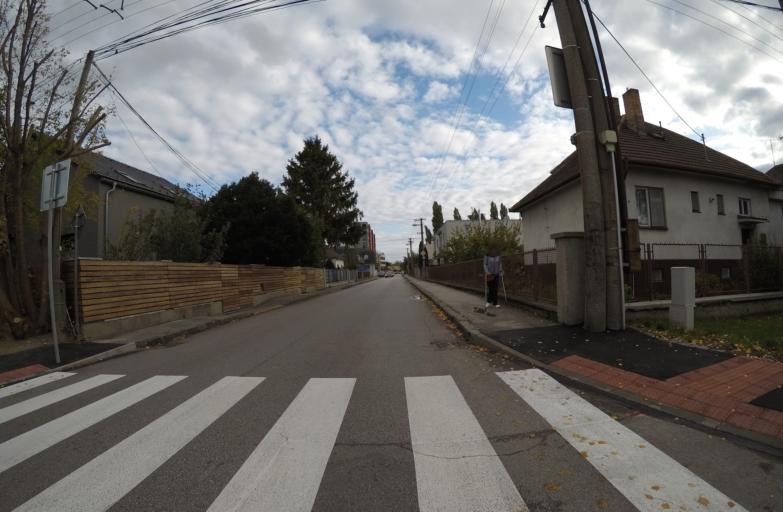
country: SK
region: Bratislavsky
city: Bratislava
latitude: 48.1683
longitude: 17.1703
